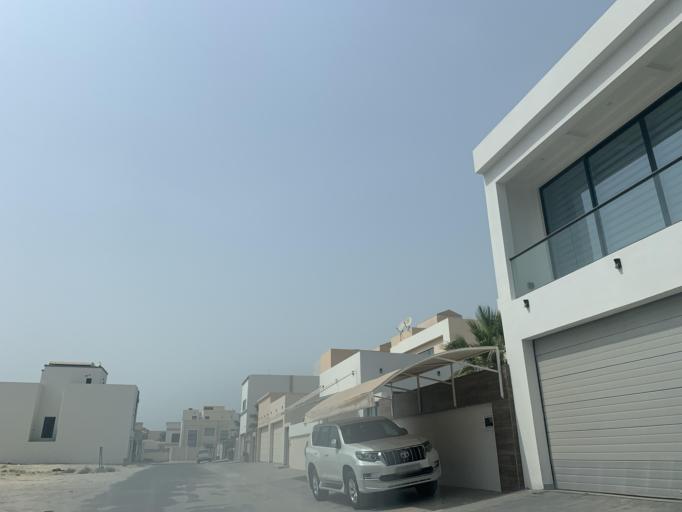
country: BH
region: Manama
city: Jidd Hafs
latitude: 26.2020
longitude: 50.4675
